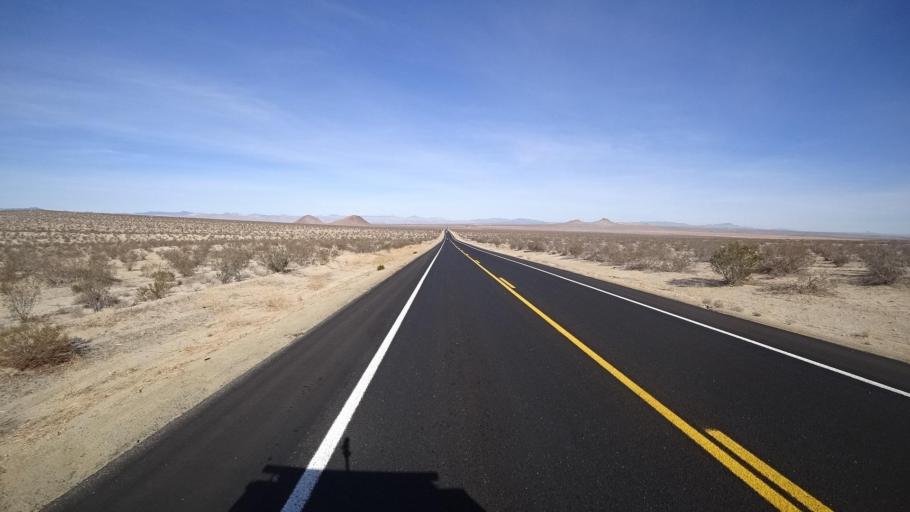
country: US
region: California
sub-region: Kern County
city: North Edwards
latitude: 35.0410
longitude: -117.9173
